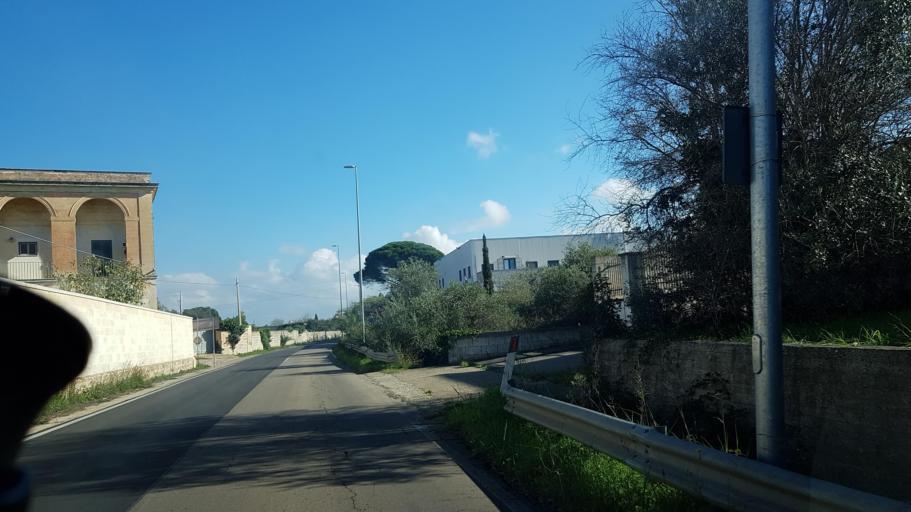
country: IT
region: Apulia
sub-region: Provincia di Lecce
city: Arnesano
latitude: 40.3357
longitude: 18.0976
